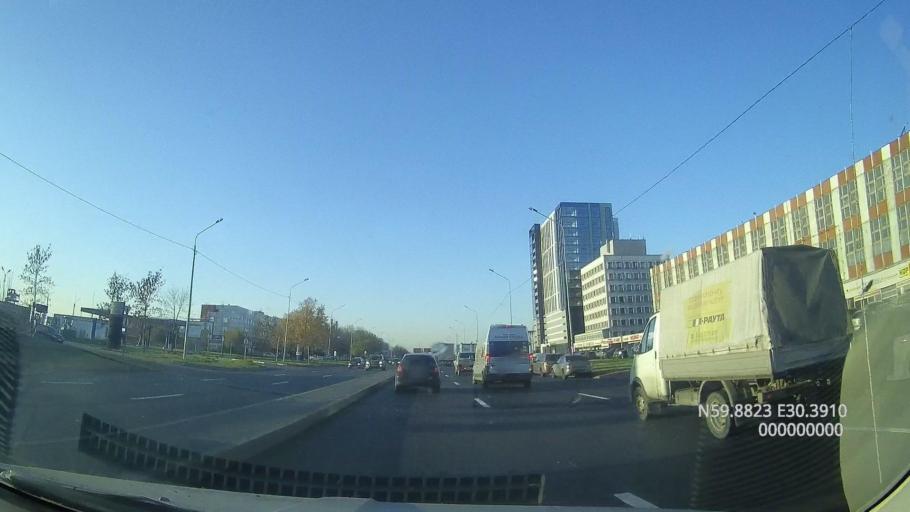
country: RU
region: St.-Petersburg
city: Kupchino
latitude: 59.8824
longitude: 30.3909
